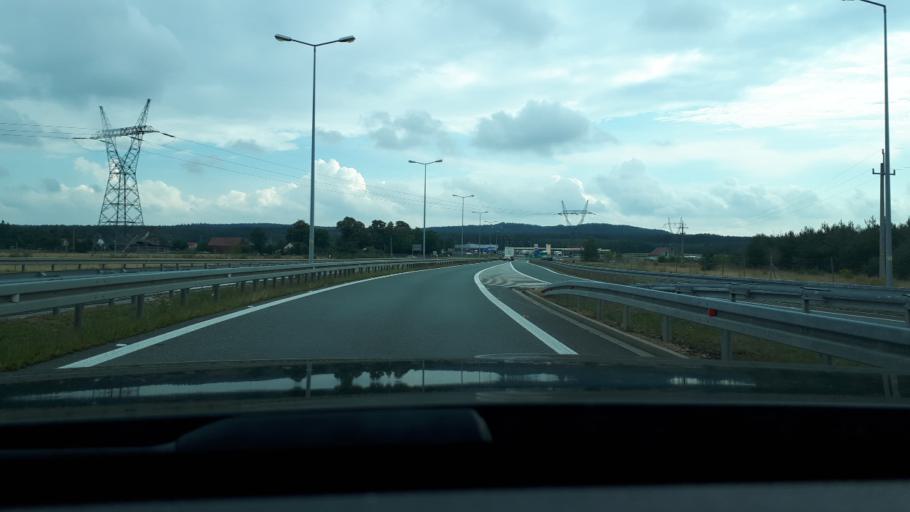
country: PL
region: Lower Silesian Voivodeship
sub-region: Powiat lubanski
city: Pisarzowice
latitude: 51.2151
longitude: 15.2417
